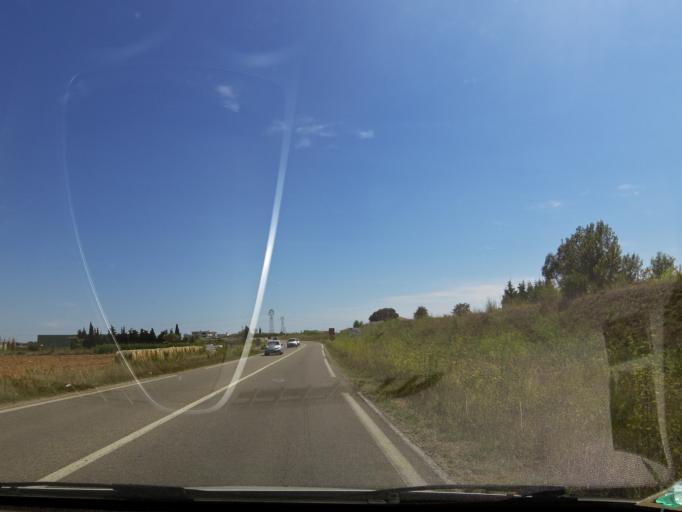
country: FR
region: Languedoc-Roussillon
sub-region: Departement de l'Herault
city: Vendargues
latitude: 43.6570
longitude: 3.9812
